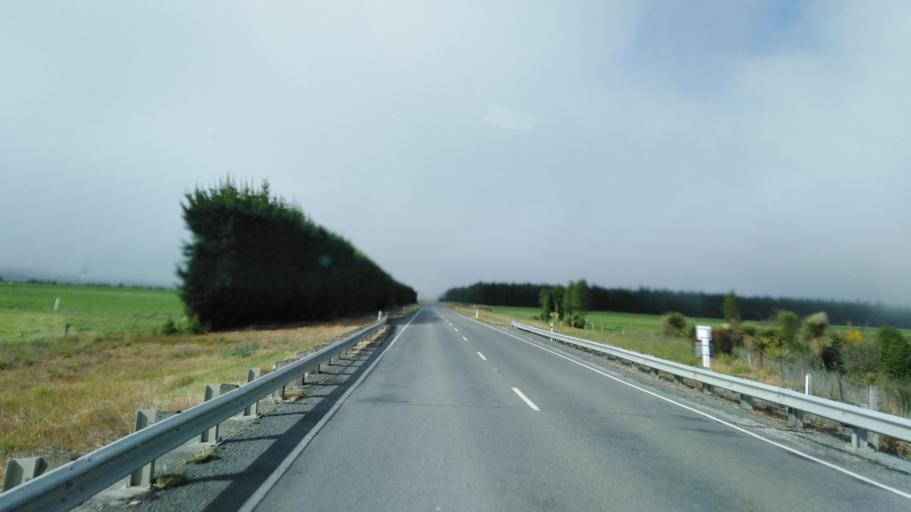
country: NZ
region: Canterbury
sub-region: Hurunui District
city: Amberley
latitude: -42.8137
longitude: 172.8164
